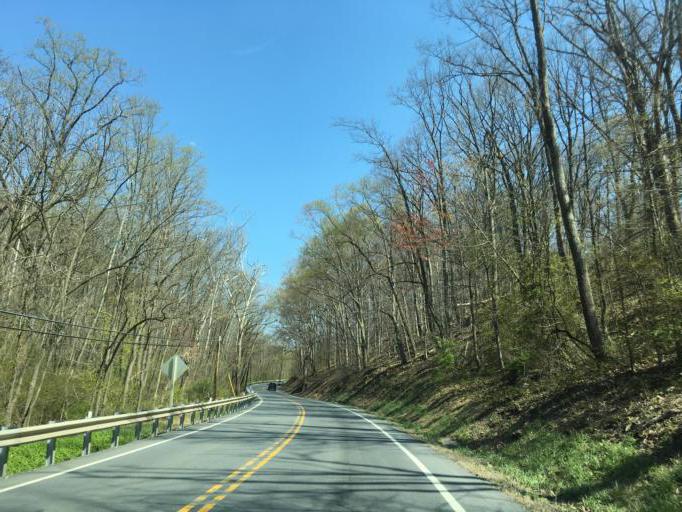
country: US
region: Maryland
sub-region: Frederick County
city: Woodsboro
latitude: 39.5287
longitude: -77.3048
